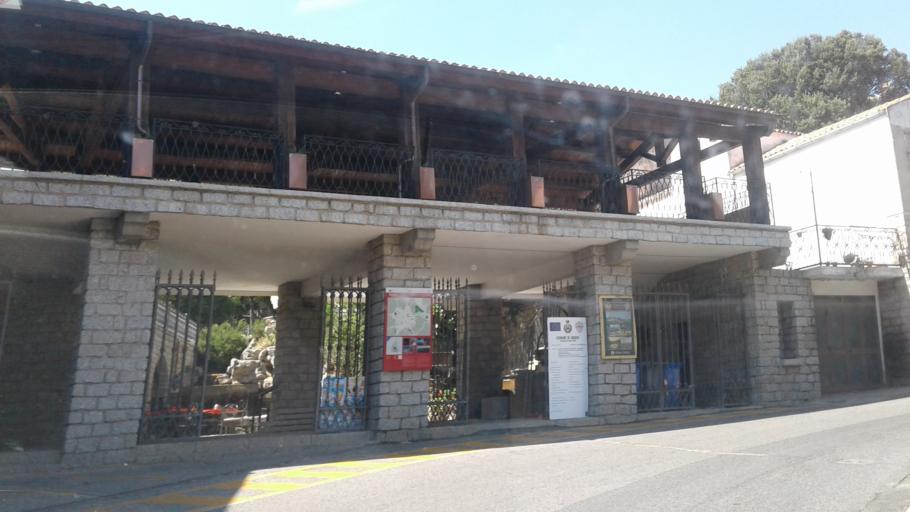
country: IT
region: Sardinia
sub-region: Provincia di Olbia-Tempio
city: Aggius
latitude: 40.9282
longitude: 9.0634
